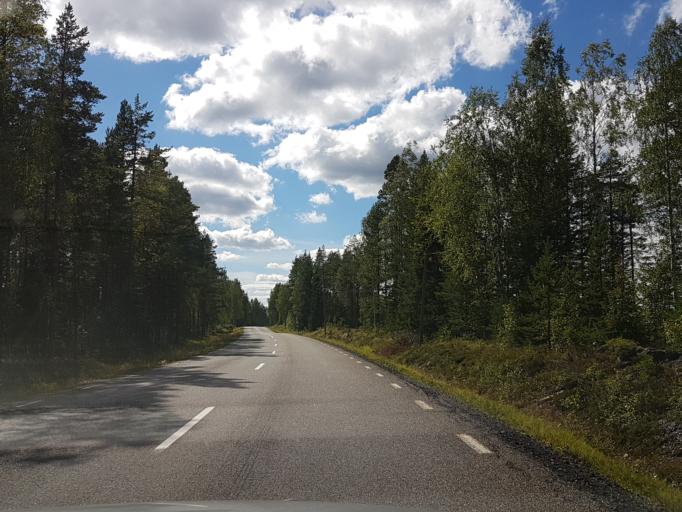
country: SE
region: Vaesterbotten
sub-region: Umea Kommun
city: Saevar
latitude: 64.1356
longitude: 20.5696
